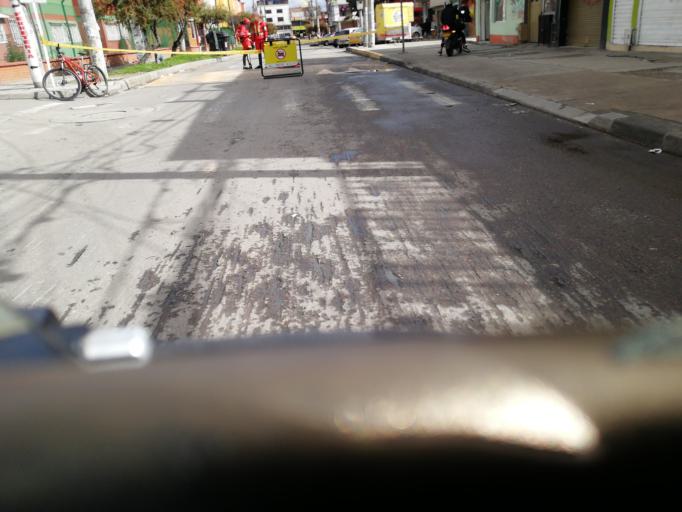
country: CO
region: Cundinamarca
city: Soacha
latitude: 4.6119
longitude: -74.1752
